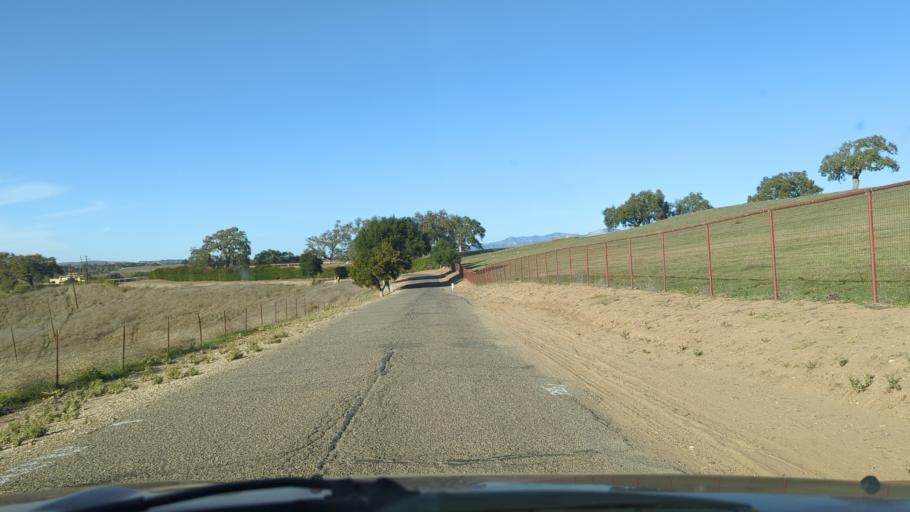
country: US
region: California
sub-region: Santa Barbara County
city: Santa Ynez
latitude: 34.5772
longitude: -120.0989
